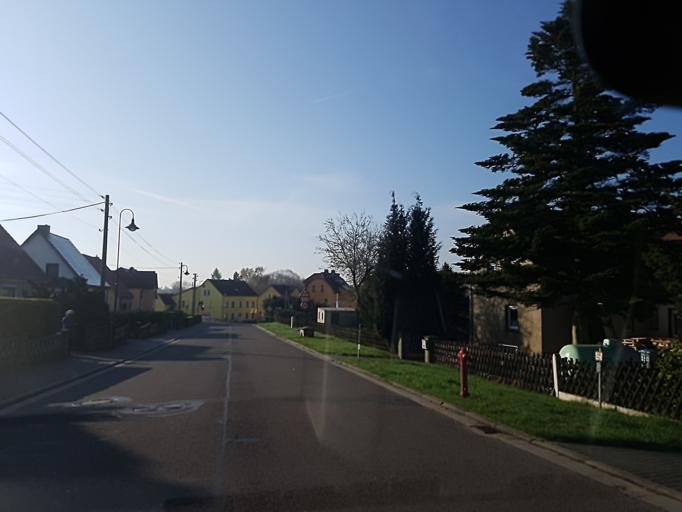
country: DE
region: Saxony
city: Mugeln
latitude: 51.2412
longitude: 13.0396
